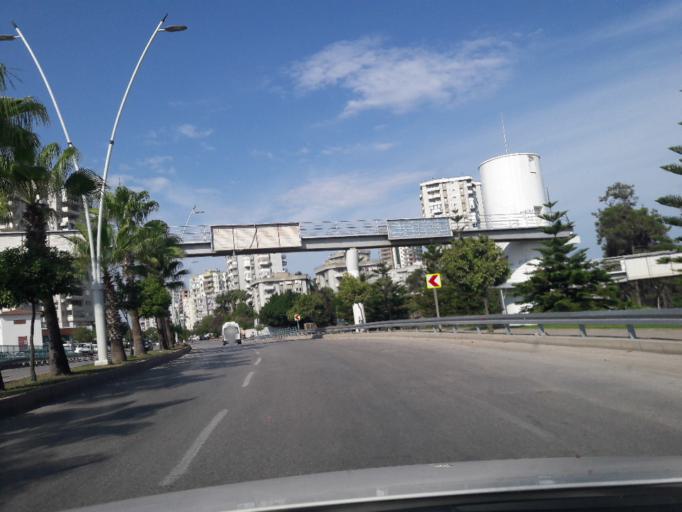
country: TR
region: Adana
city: Adana
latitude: 37.0143
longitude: 35.3271
